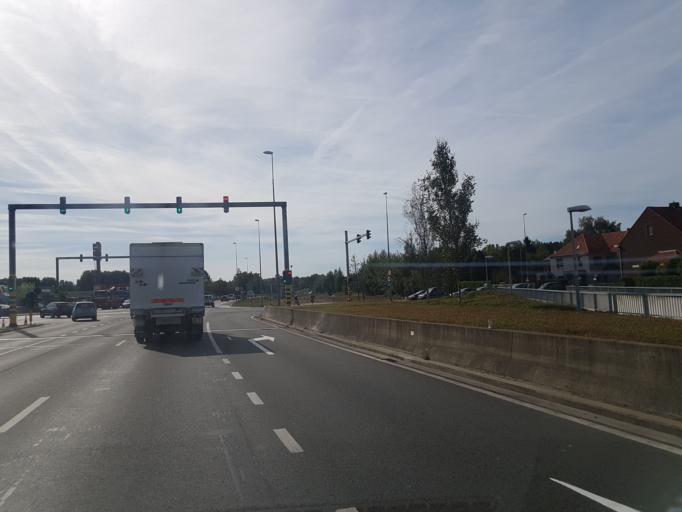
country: BE
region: Flanders
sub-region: Provincie Antwerpen
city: Mol
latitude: 51.1801
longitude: 5.1251
